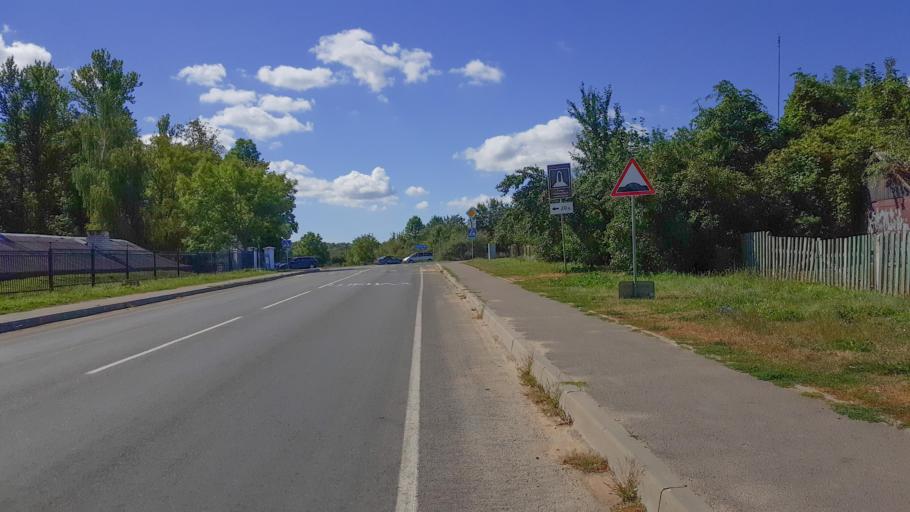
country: BY
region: Brest
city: Vysokaye
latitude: 52.3705
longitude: 23.3660
